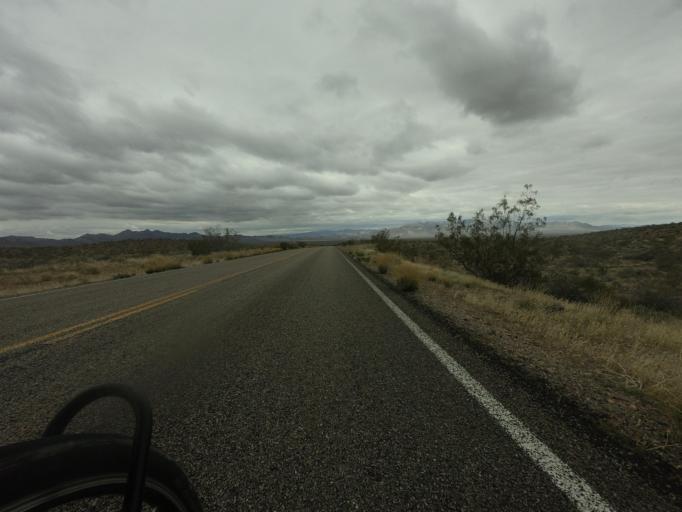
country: US
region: Nevada
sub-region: Nye County
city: Beatty
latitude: 36.8089
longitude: -116.9114
